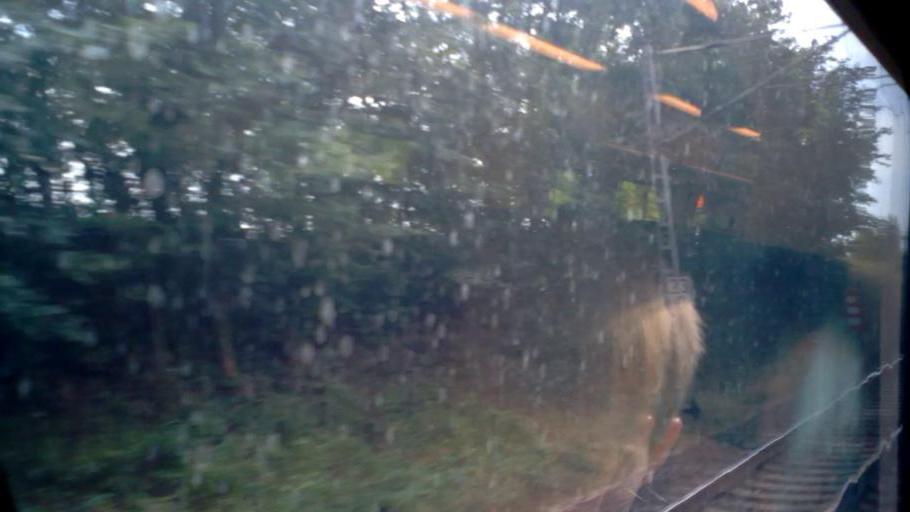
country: DE
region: Brandenburg
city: Grossbeeren
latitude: 52.3428
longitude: 13.3524
